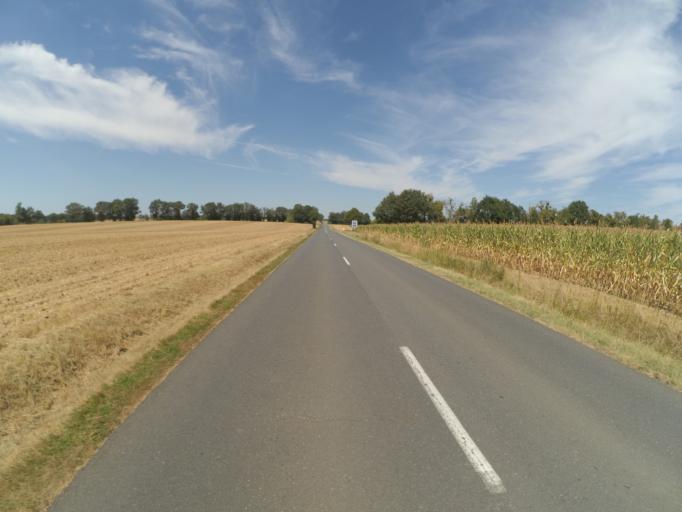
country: FR
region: Poitou-Charentes
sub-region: Departement de la Vienne
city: Usson-du-Poitou
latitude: 46.1918
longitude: 0.5384
